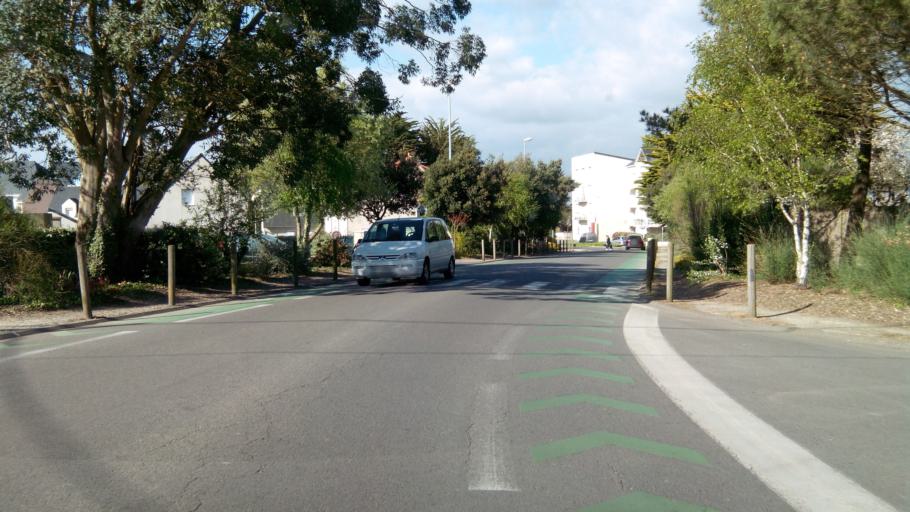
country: FR
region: Pays de la Loire
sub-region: Departement de la Loire-Atlantique
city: Pornichet
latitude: 47.2588
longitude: -2.3358
